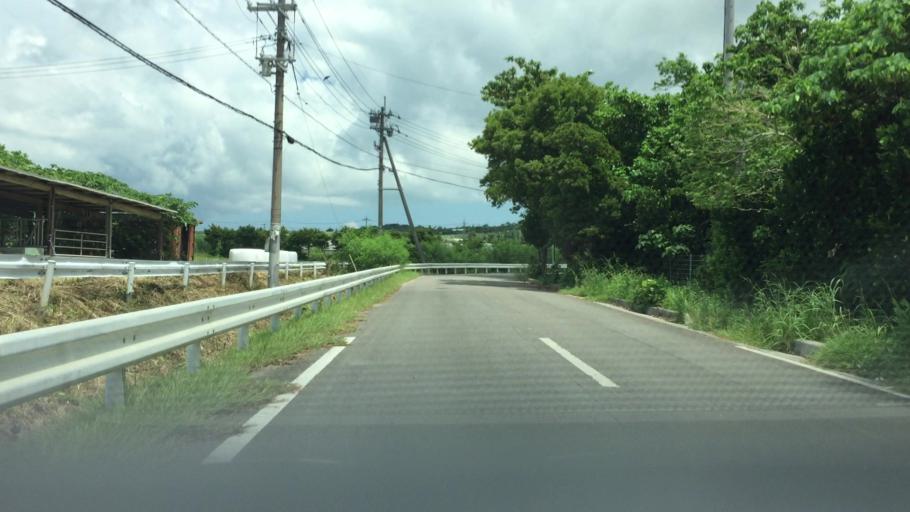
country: JP
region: Okinawa
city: Ishigaki
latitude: 24.3577
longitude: 124.1385
